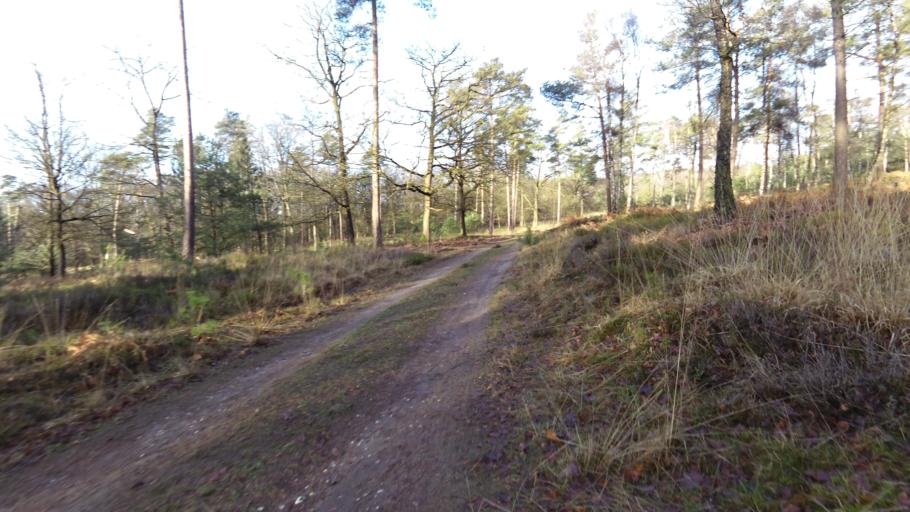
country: NL
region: Gelderland
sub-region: Gemeente Apeldoorn
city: Apeldoorn
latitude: 52.2374
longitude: 5.8850
